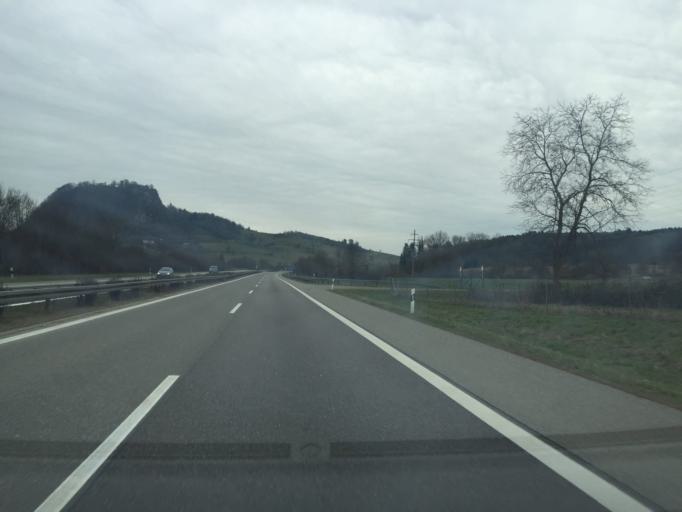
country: DE
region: Baden-Wuerttemberg
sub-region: Freiburg Region
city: Singen
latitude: 47.7788
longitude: 8.8188
